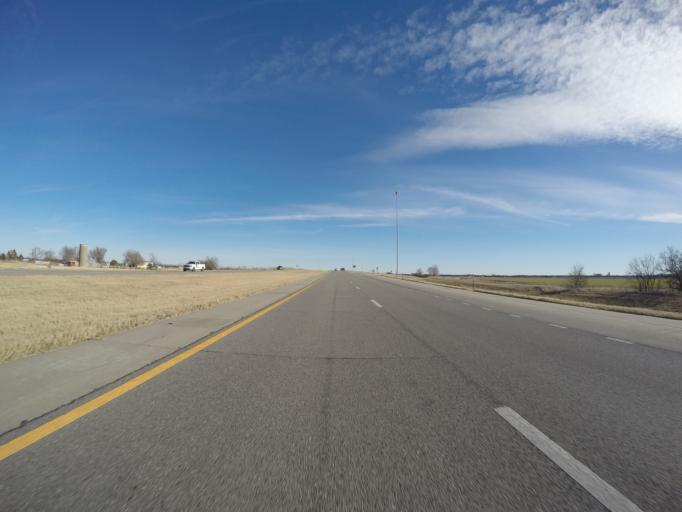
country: US
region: Kansas
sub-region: McPherson County
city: Moundridge
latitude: 38.2328
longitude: -97.5228
